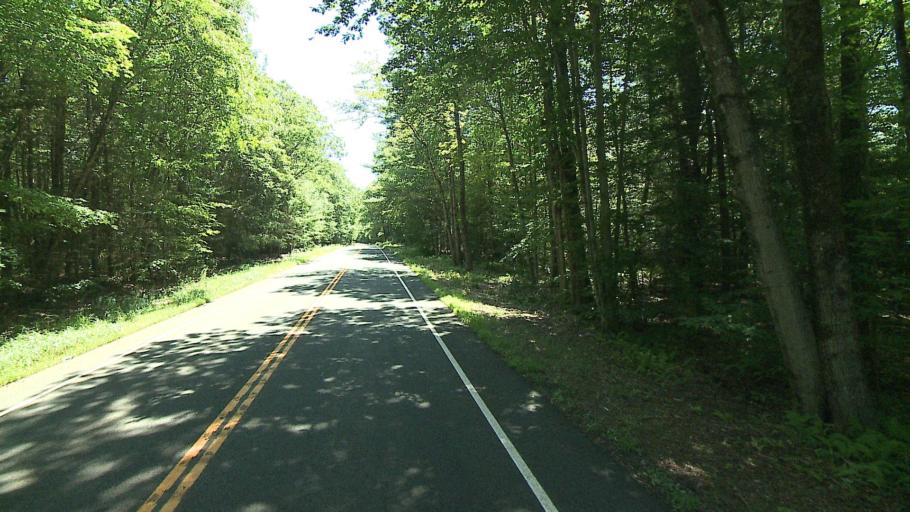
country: US
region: Connecticut
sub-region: Litchfield County
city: New Hartford Center
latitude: 41.9678
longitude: -72.9801
